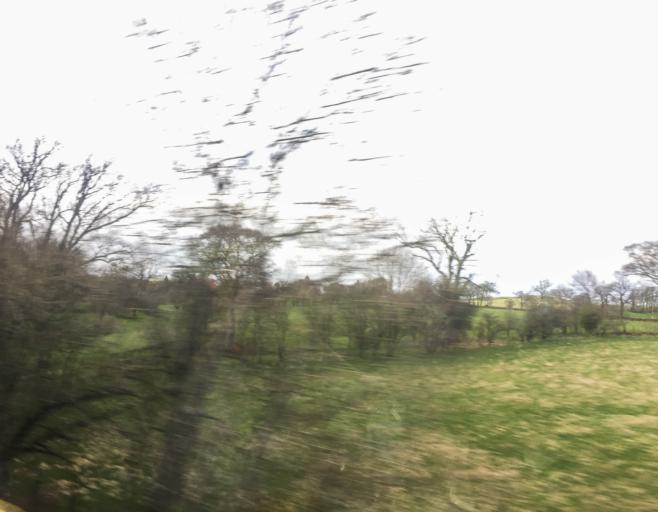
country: GB
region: Scotland
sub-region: Dumfries and Galloway
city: Lockerbie
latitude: 55.1000
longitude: -3.3256
